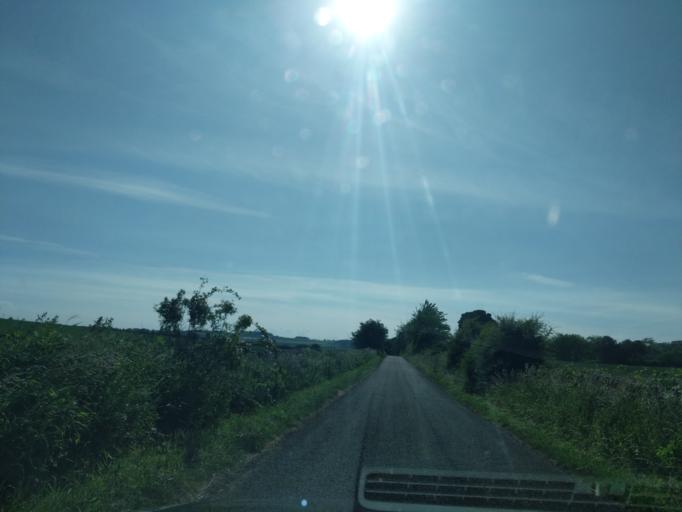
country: GB
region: Scotland
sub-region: Fife
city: Pathhead
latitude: 55.8772
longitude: -2.9539
